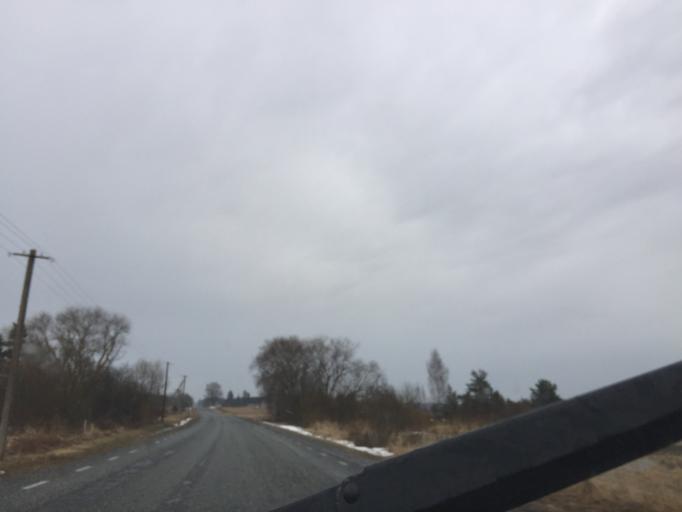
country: EE
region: Saare
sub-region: Orissaare vald
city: Orissaare
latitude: 58.5643
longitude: 23.0424
